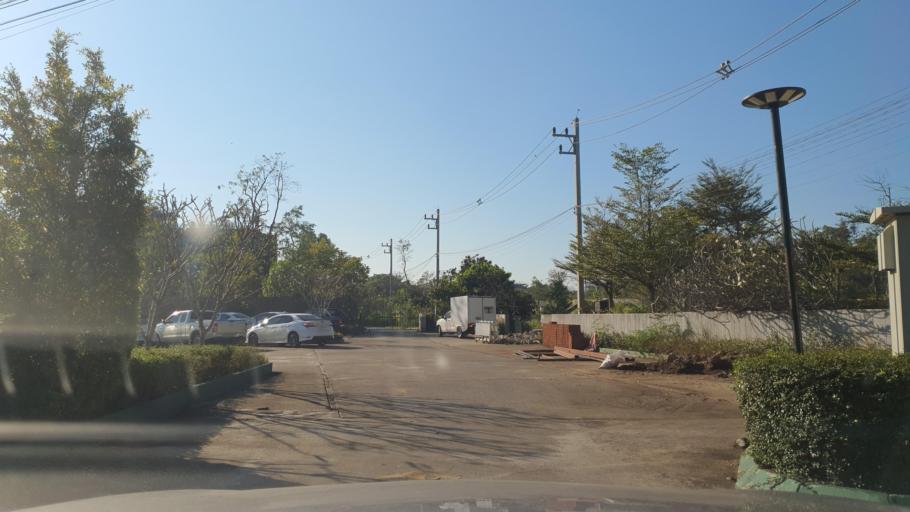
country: TH
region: Chiang Mai
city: Hang Dong
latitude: 18.6950
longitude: 98.9576
